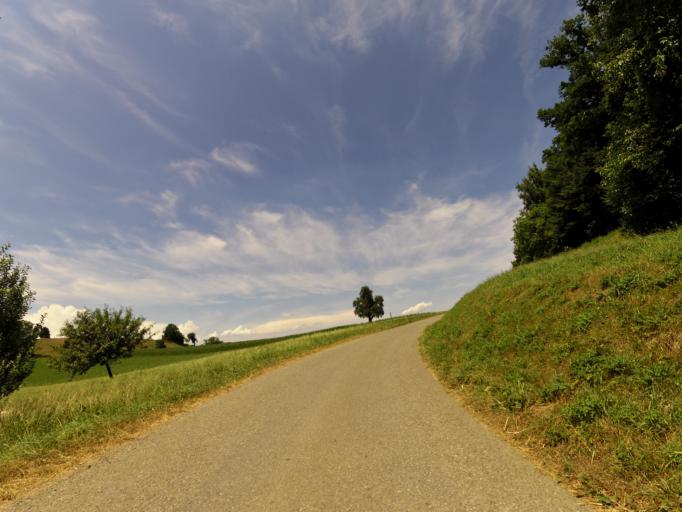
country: CH
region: Aargau
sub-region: Bezirk Bremgarten
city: Bremgarten
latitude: 47.3298
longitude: 8.3516
